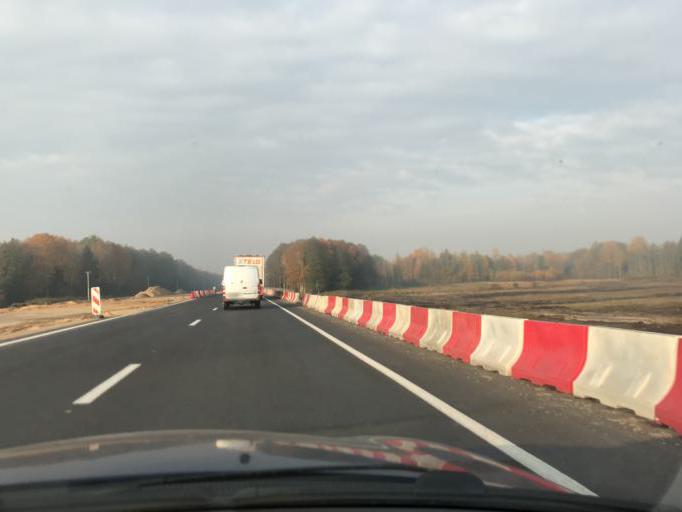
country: BY
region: Grodnenskaya
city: Lida
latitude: 53.8287
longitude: 25.4182
